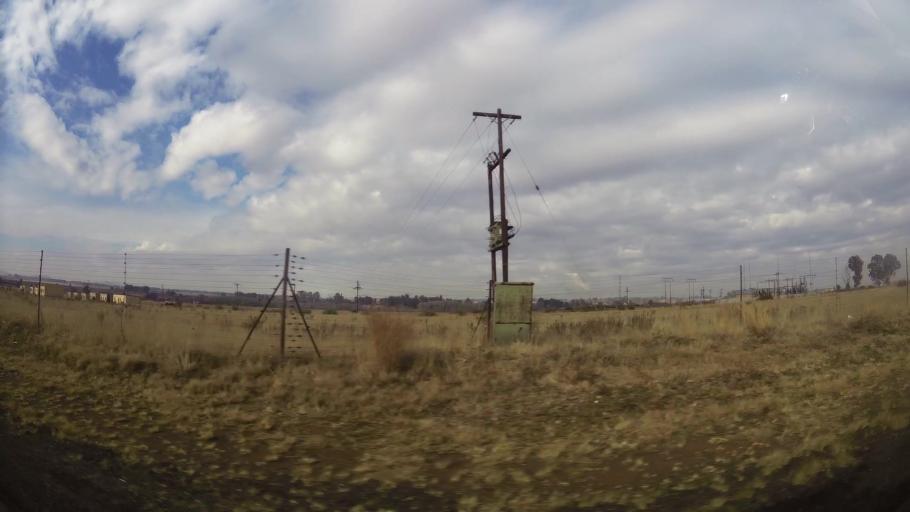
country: ZA
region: Gauteng
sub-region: Sedibeng District Municipality
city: Meyerton
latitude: -26.5582
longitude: 28.0530
